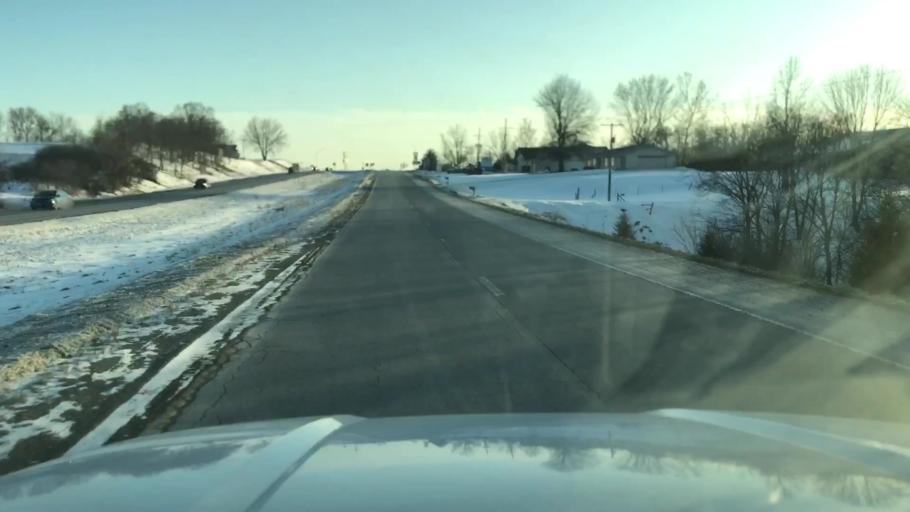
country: US
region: Missouri
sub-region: Andrew County
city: Country Club Village
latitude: 39.8634
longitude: -94.8090
